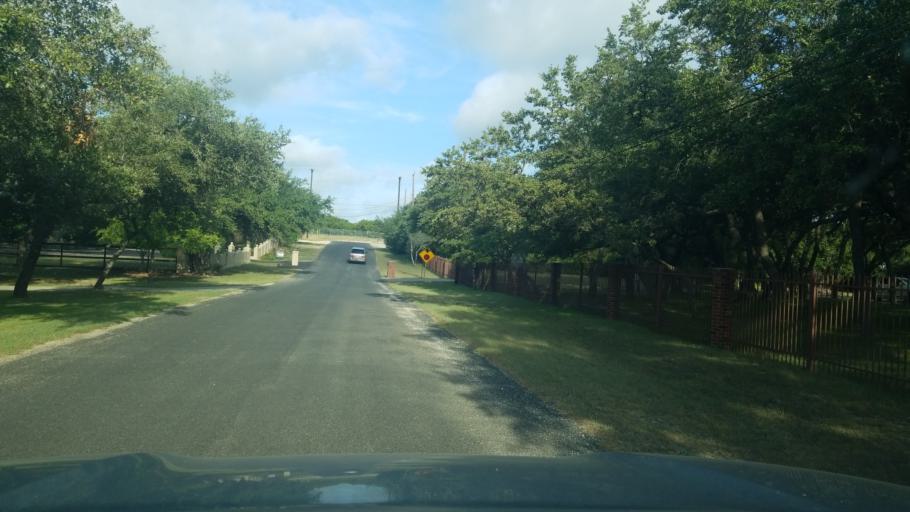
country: US
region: Texas
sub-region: Bexar County
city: Timberwood Park
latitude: 29.6955
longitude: -98.5199
